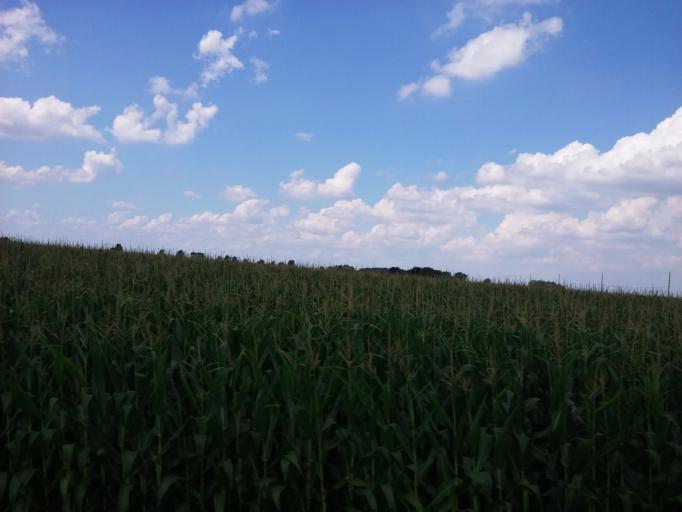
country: US
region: Ohio
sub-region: Wood County
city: Bowling Green
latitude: 41.3743
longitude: -83.5918
